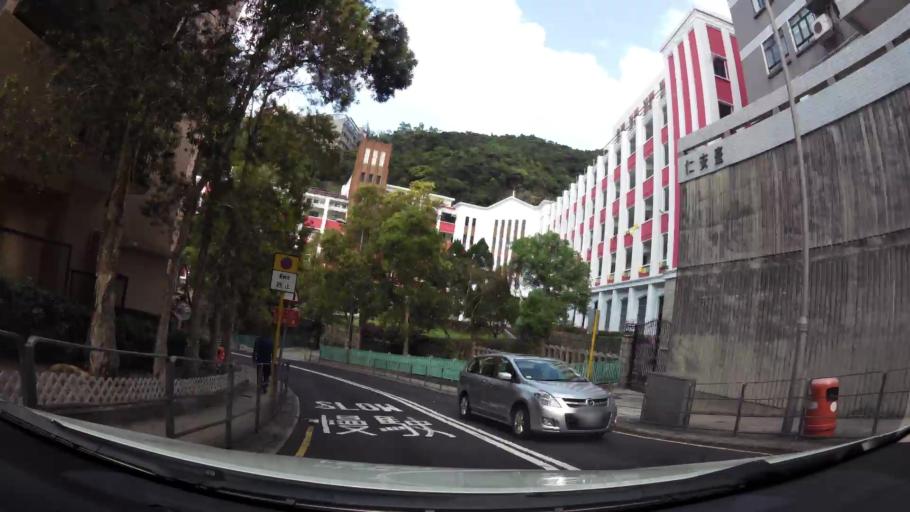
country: HK
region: Wanchai
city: Wan Chai
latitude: 22.2634
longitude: 114.1898
